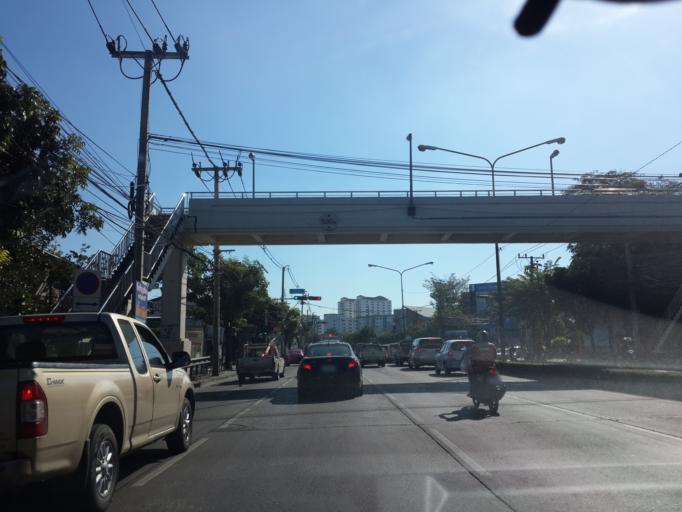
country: TH
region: Bangkok
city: Bang Kapi
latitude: 13.7811
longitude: 100.6456
